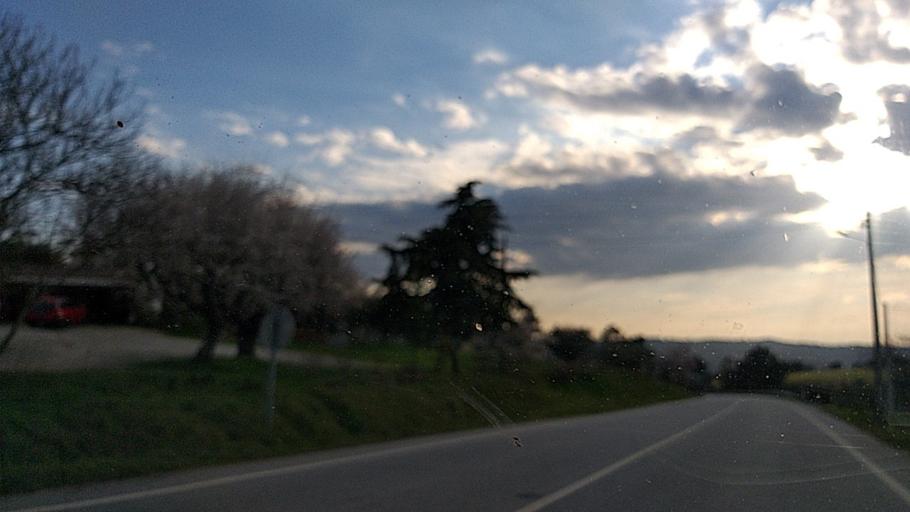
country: ES
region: Castille and Leon
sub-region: Provincia de Salamanca
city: Aldea del Obispo
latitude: 40.7132
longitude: -6.9117
